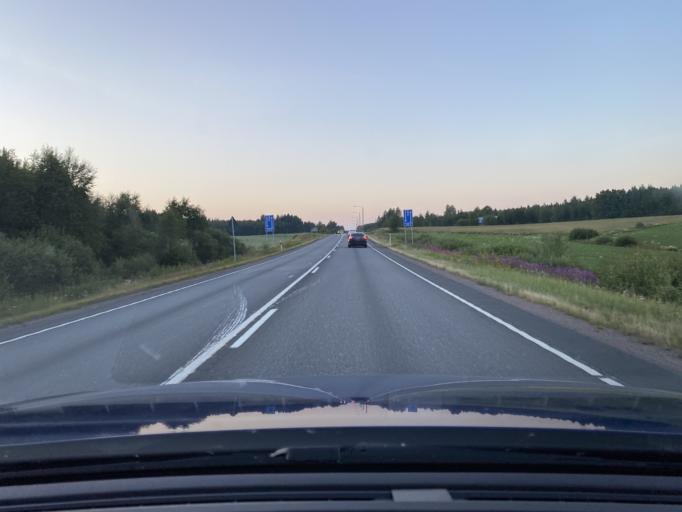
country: FI
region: Pirkanmaa
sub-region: Luoteis-Pirkanmaa
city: Ikaalinen
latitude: 61.8740
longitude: 22.9668
